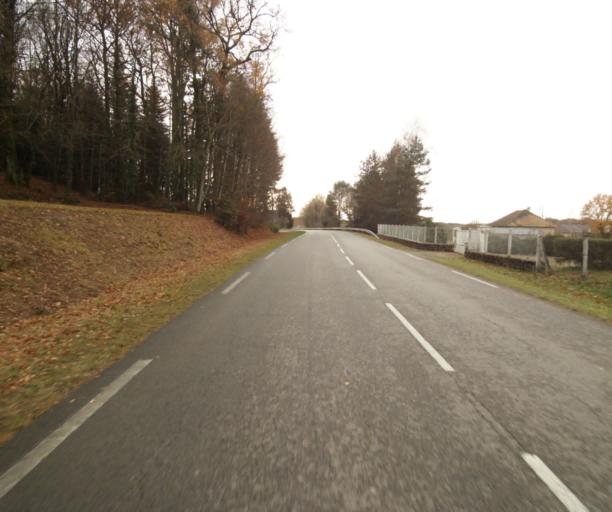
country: FR
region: Limousin
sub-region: Departement de la Correze
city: Sainte-Fortunade
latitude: 45.1755
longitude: 1.7565
